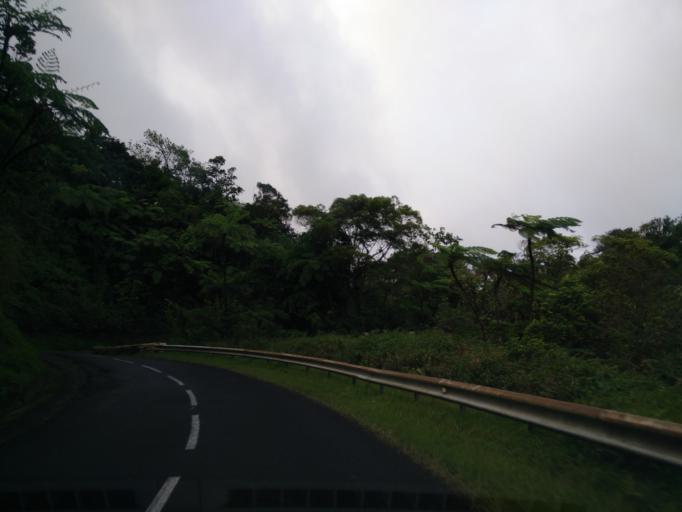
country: MQ
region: Martinique
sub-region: Martinique
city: Le Morne-Rouge
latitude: 14.7258
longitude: -61.1031
